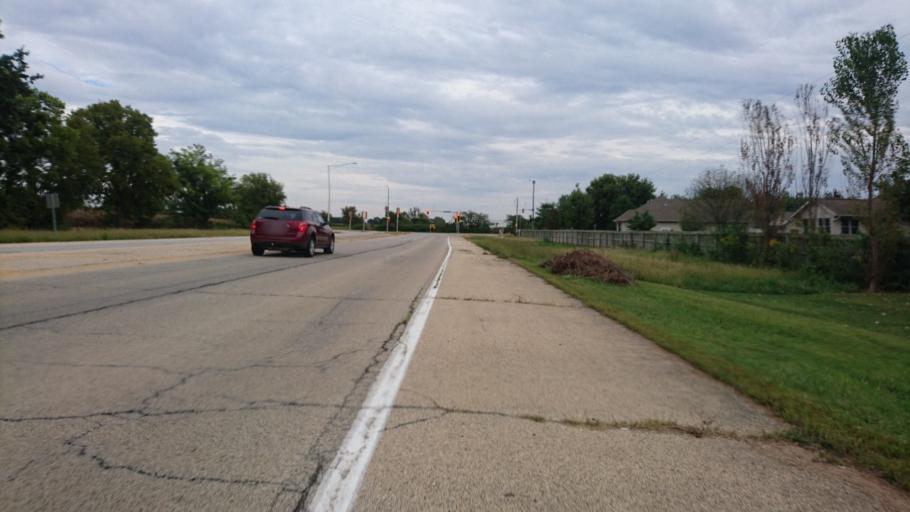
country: US
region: Illinois
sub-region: Sangamon County
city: Chatham
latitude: 39.6736
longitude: -89.6501
